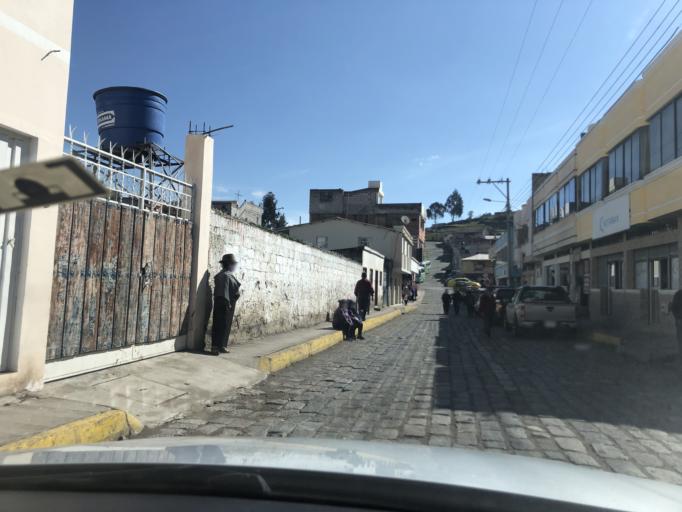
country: EC
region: Chimborazo
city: Riobamba
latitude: -1.7011
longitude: -78.7717
